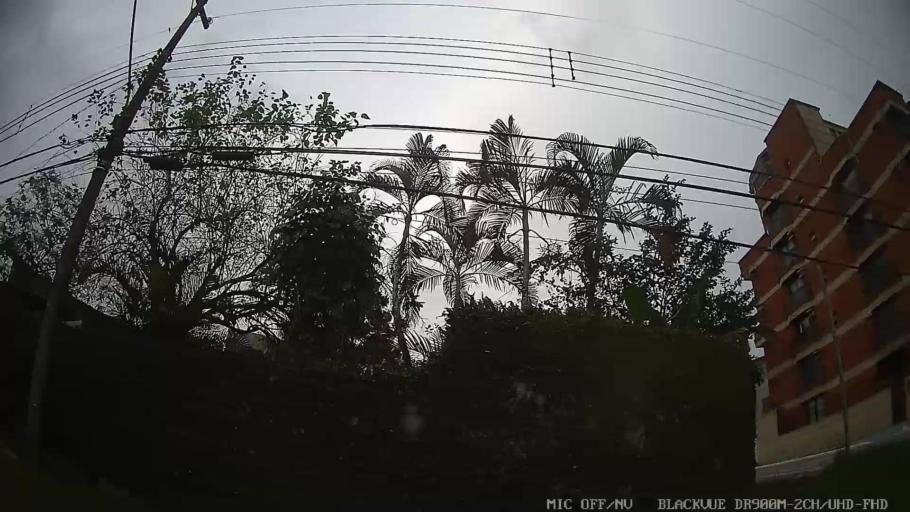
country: BR
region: Sao Paulo
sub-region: Guaruja
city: Guaruja
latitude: -23.9790
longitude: -46.2280
